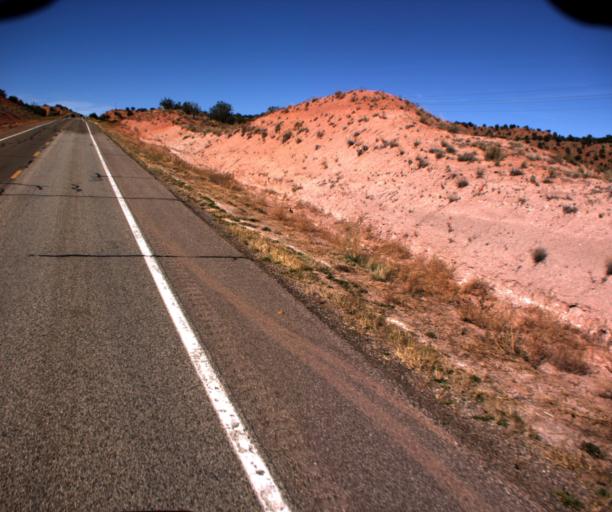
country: US
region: Arizona
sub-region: Mohave County
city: Colorado City
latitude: 36.8792
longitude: -112.8879
